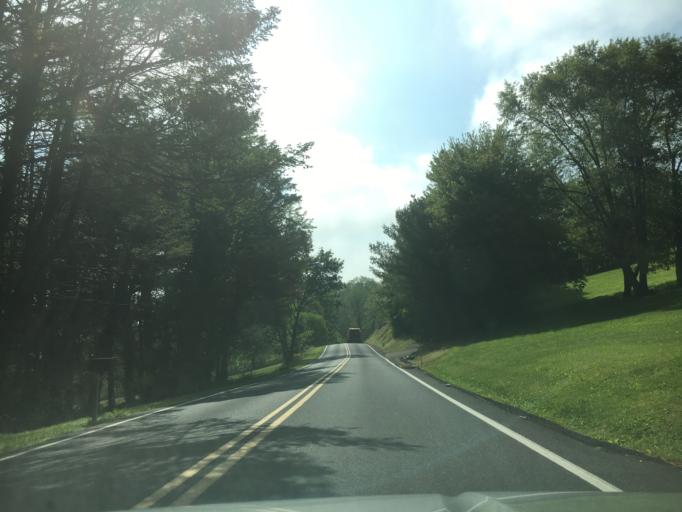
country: US
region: Pennsylvania
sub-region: Berks County
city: New Berlinville
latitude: 40.3469
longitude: -75.6424
